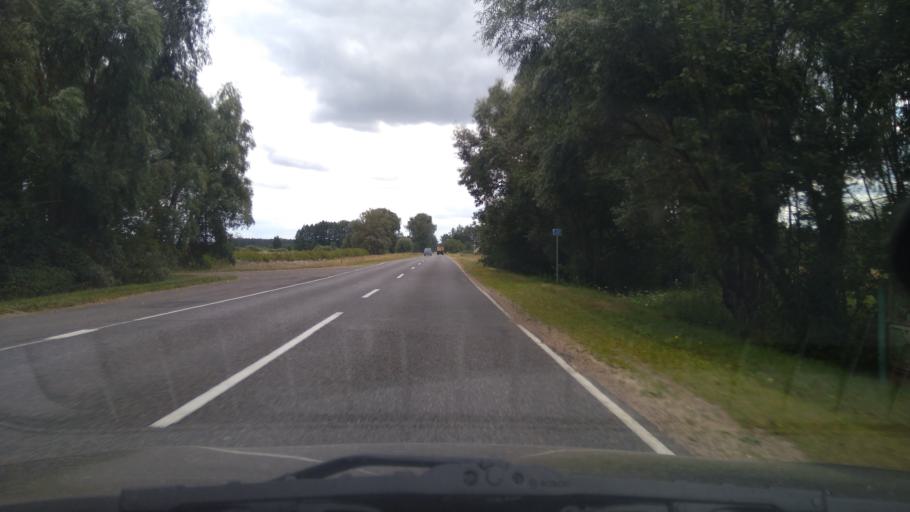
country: BY
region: Brest
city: Byelaazyorsk
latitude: 52.4192
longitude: 25.2346
